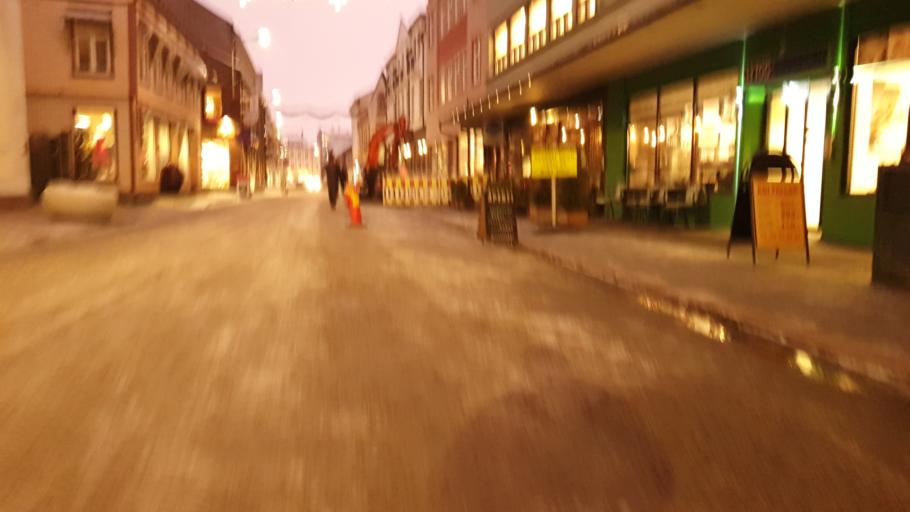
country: NO
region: Buskerud
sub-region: Drammen
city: Drammen
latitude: 59.7393
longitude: 10.2032
